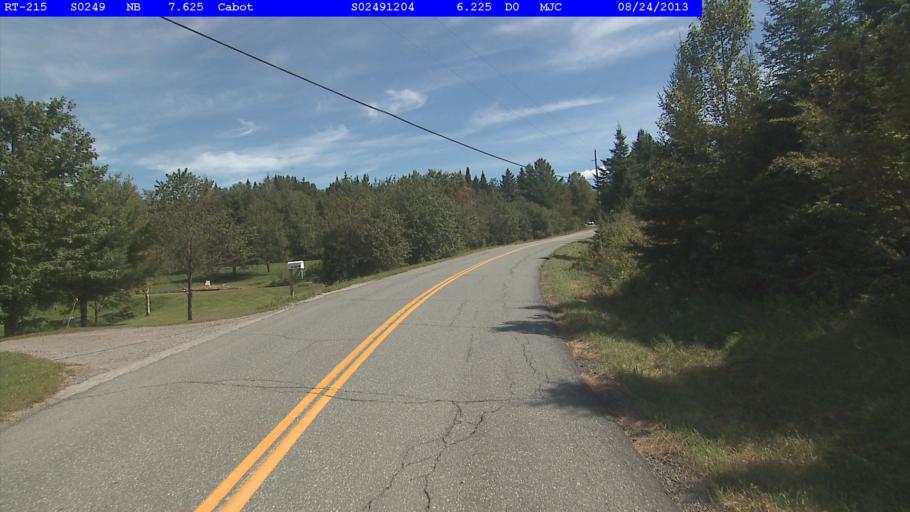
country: US
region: Vermont
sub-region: Caledonia County
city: Hardwick
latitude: 44.4389
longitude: -72.2784
